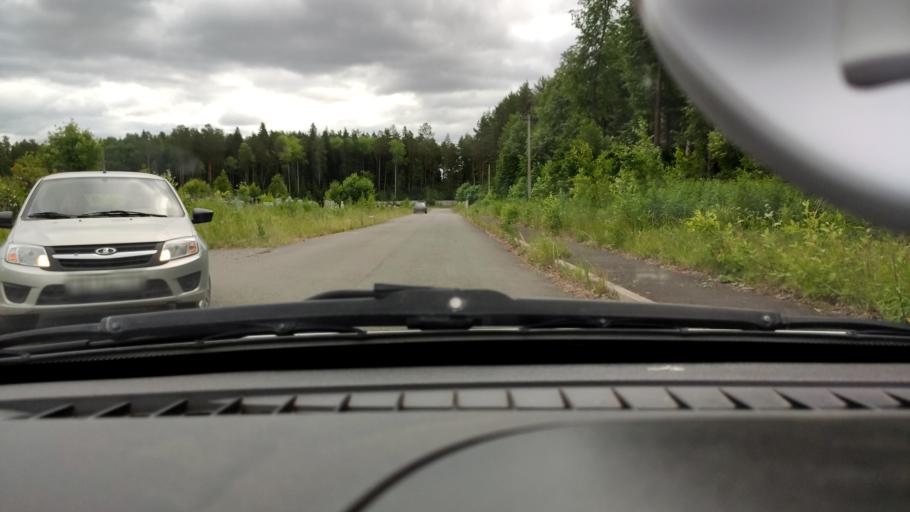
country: RU
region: Perm
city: Kondratovo
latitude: 58.0614
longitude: 56.1572
